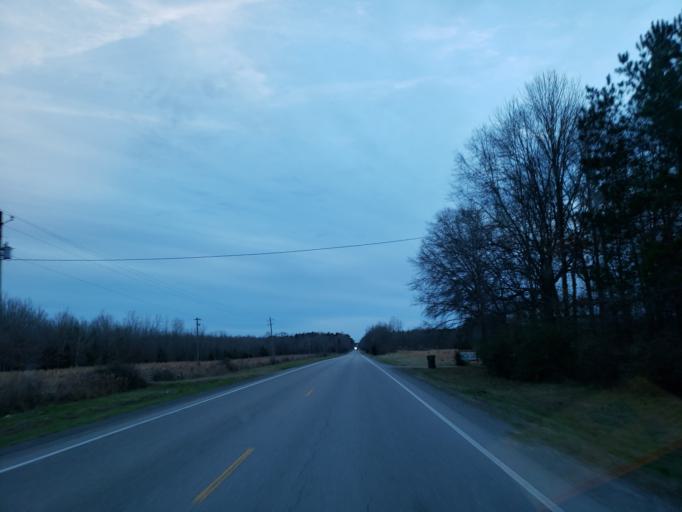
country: US
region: Alabama
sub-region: Sumter County
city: Livingston
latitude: 32.8290
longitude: -88.3095
